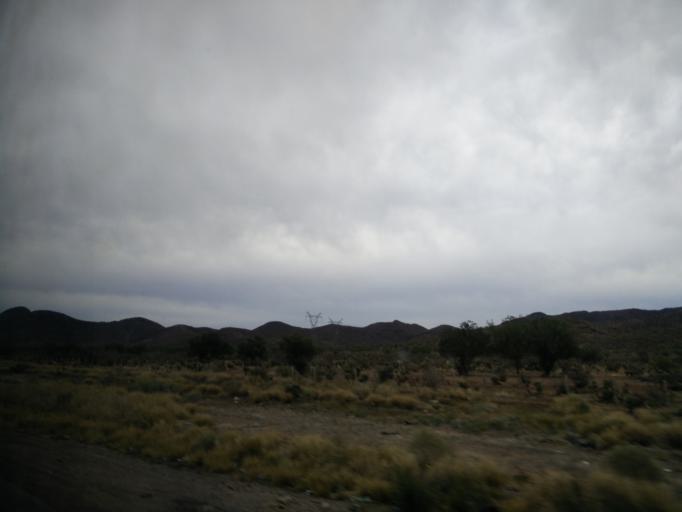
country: MX
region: Sonora
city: Hermosillo
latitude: 28.6183
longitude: -111.0151
